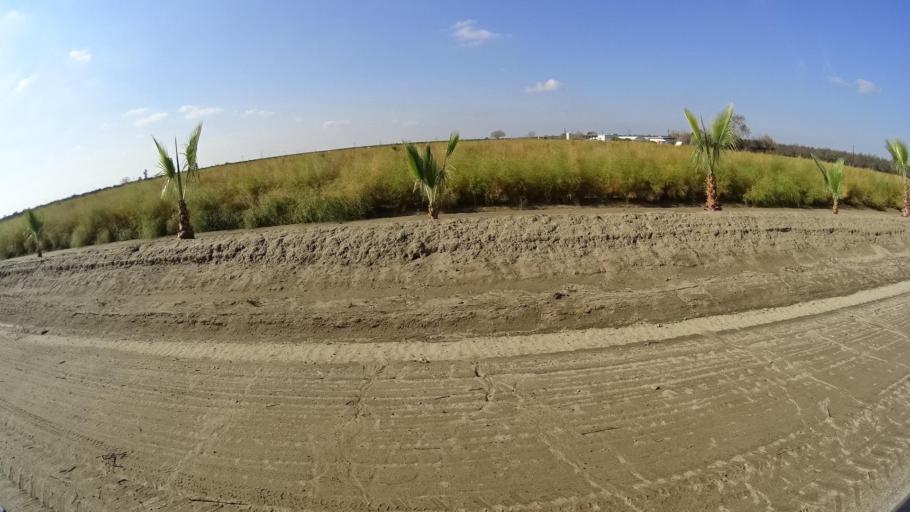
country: US
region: California
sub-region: Kern County
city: Arvin
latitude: 35.2297
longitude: -118.7884
